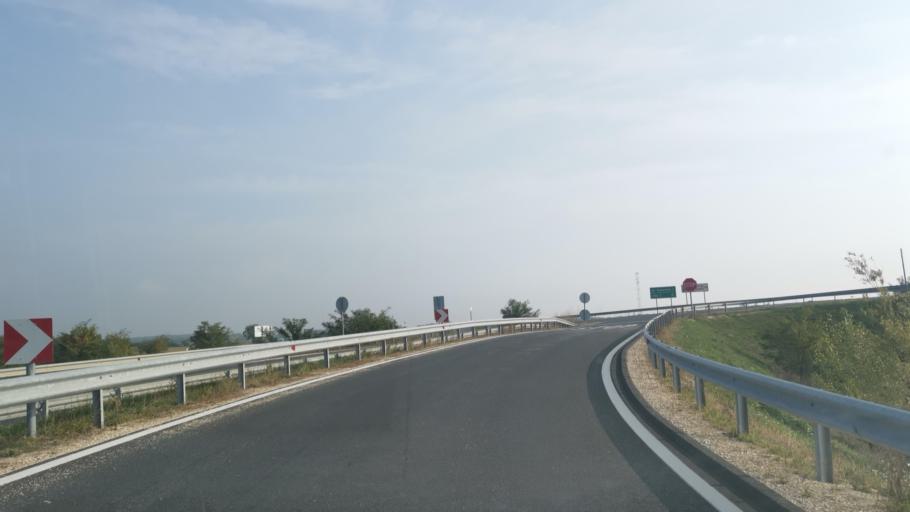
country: HU
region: Vas
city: Vep
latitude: 47.2570
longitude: 16.7179
